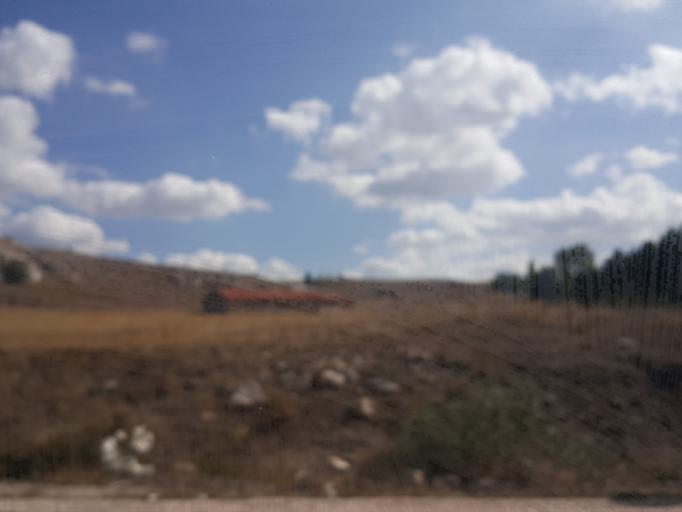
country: TR
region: Tokat
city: Artova
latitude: 40.1389
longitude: 36.3579
